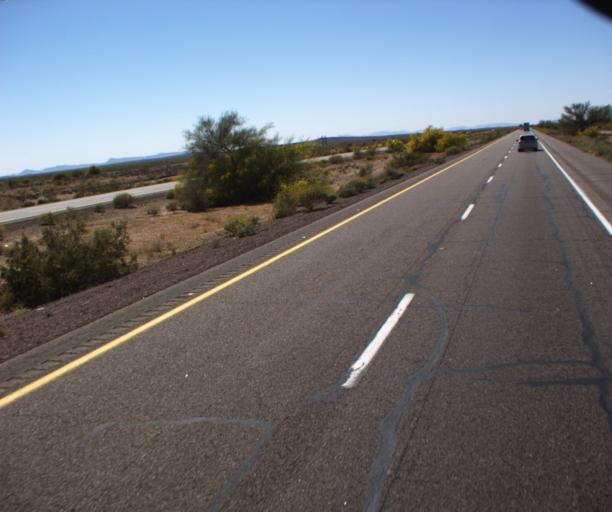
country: US
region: Arizona
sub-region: Maricopa County
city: Gila Bend
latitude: 32.8663
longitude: -113.1553
